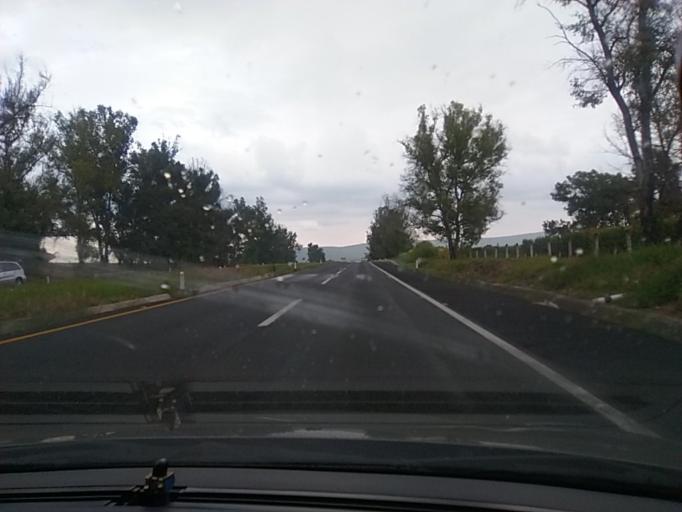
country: MX
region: Jalisco
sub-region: Zapotlan del Rey
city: Zapotlan del Rey
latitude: 20.4590
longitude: -102.8973
